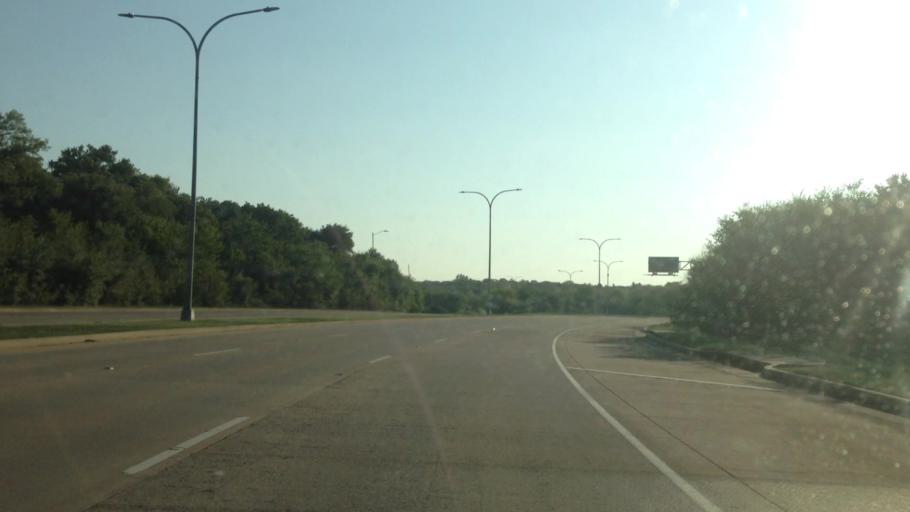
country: US
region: Texas
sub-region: Tarrant County
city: Pantego
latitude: 32.7374
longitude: -97.1778
